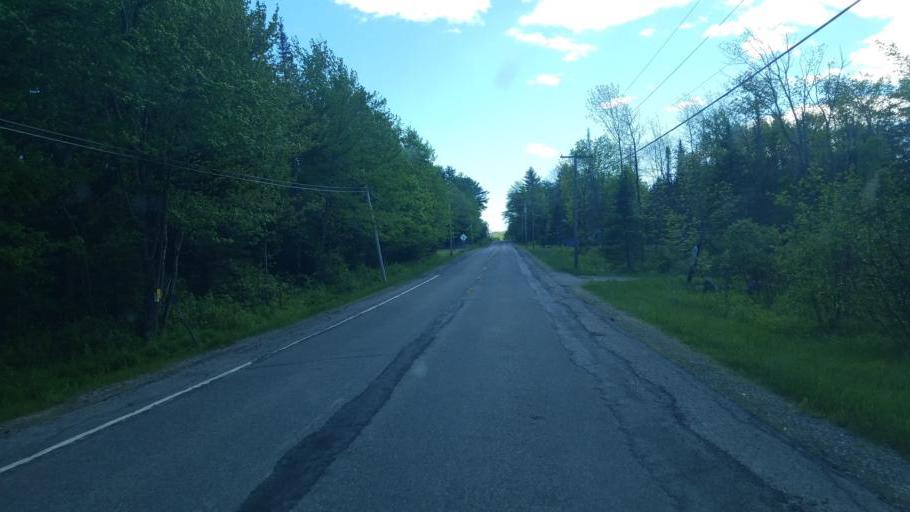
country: US
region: New York
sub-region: Fulton County
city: Gloversville
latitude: 43.1221
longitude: -74.5021
